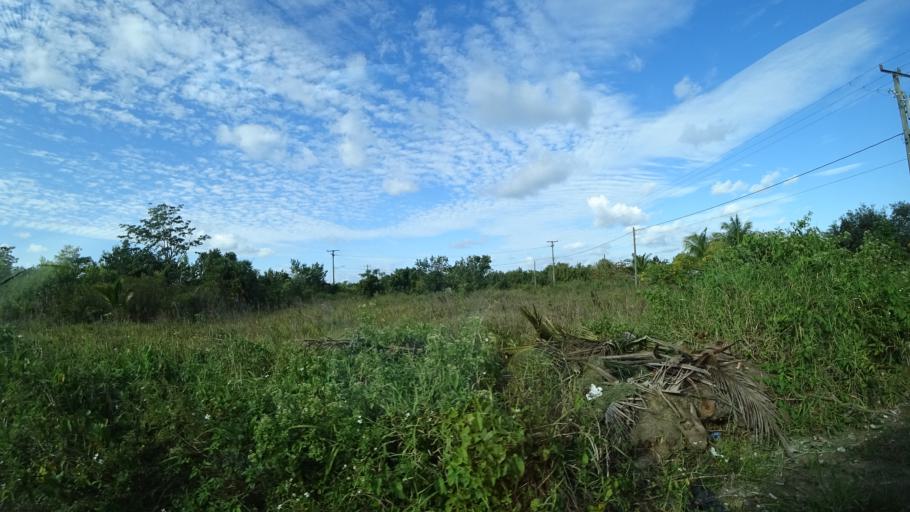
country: BZ
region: Belize
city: Belize City
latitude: 17.5552
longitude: -88.3998
